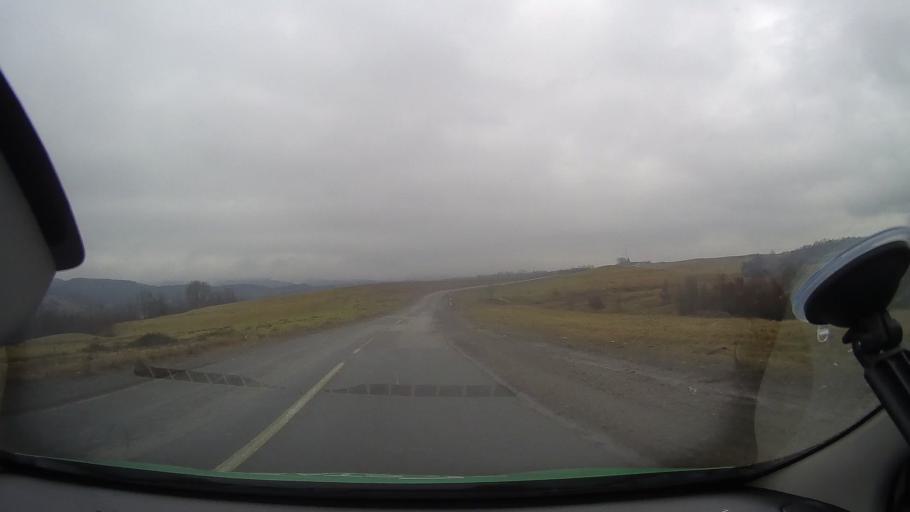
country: RO
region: Arad
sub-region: Comuna Halmagiu
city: Halmagiu
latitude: 46.2877
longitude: 22.5580
